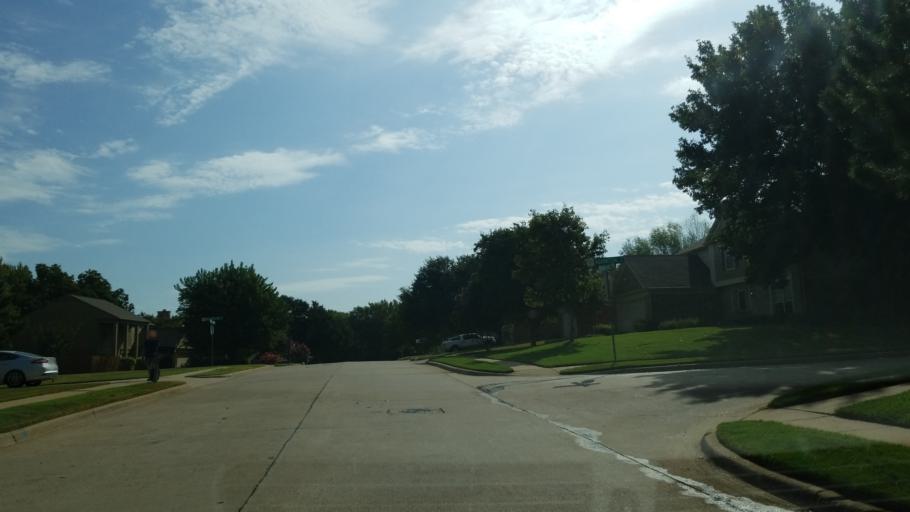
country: US
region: Texas
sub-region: Tarrant County
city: Grapevine
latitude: 32.8901
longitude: -97.0857
